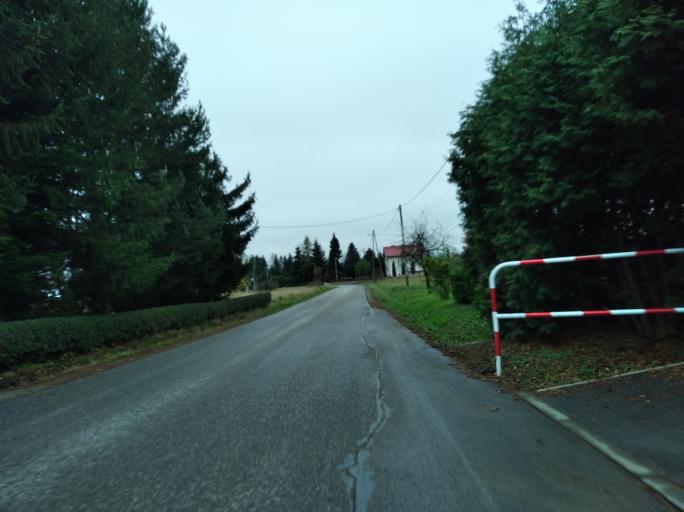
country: PL
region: Subcarpathian Voivodeship
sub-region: Powiat krosnienski
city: Odrzykon
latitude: 49.7293
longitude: 21.7662
